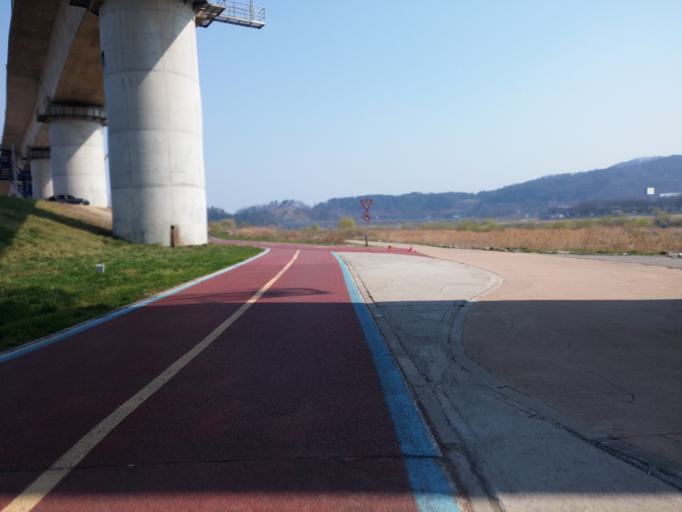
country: KR
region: Daejeon
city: Songgang-dong
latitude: 36.4104
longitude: 127.4152
